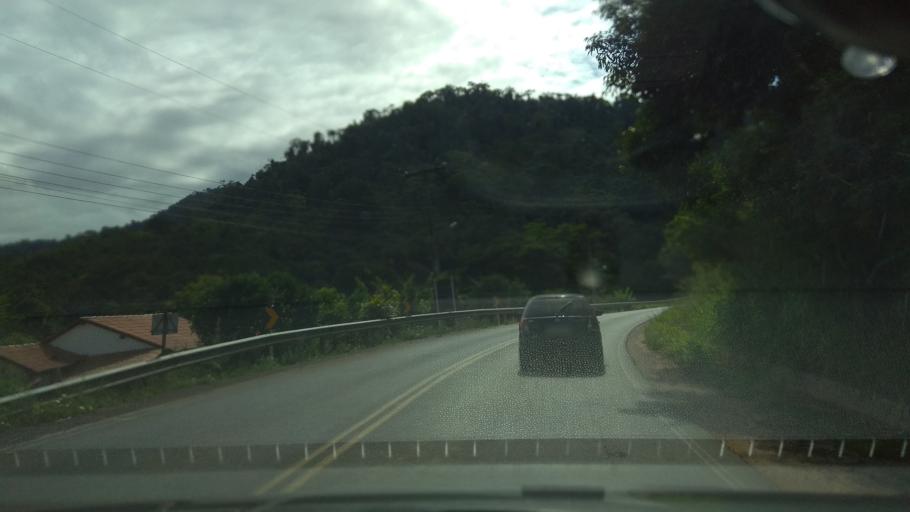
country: BR
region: Bahia
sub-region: Ubaira
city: Ubaira
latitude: -13.2583
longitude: -39.6174
